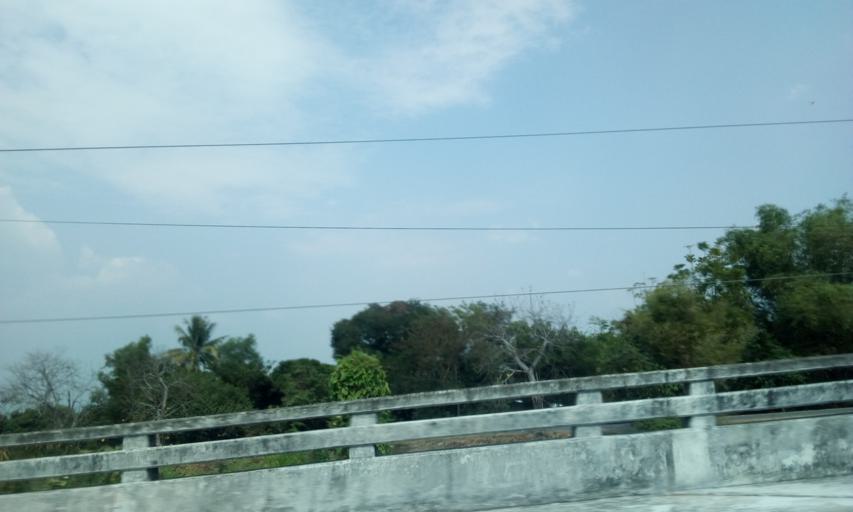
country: TH
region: Nakhon Nayok
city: Nakhon Nayok
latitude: 14.2030
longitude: 101.1899
